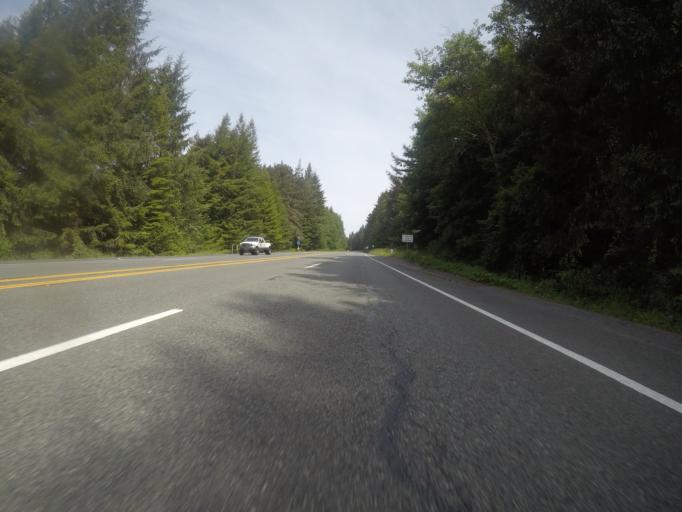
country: US
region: California
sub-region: Del Norte County
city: Bertsch-Oceanview
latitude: 41.4712
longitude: -124.0420
